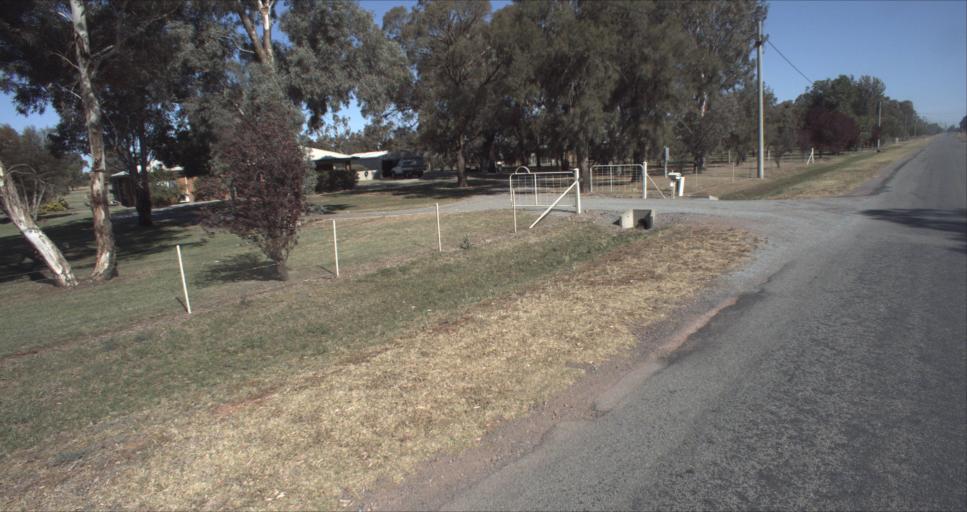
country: AU
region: New South Wales
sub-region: Leeton
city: Leeton
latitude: -34.5375
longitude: 146.4197
